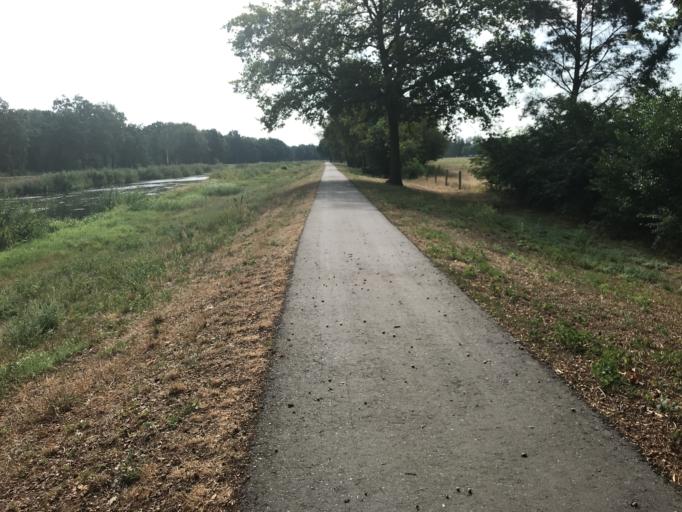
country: DE
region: Brandenburg
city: Schilda
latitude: 51.5843
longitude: 13.3347
